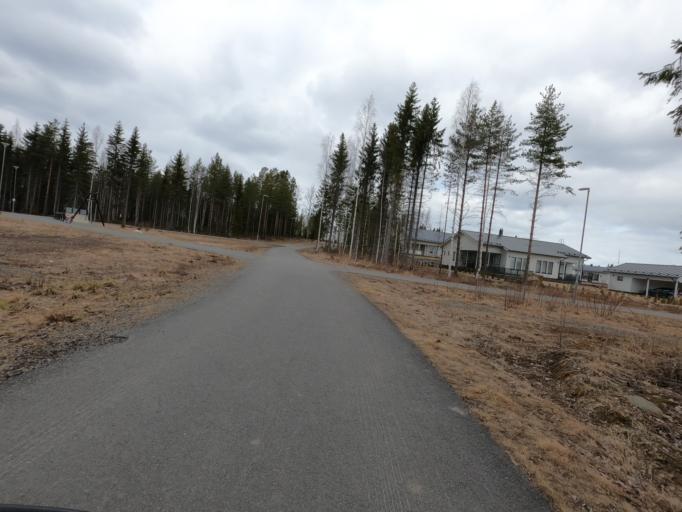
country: FI
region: North Karelia
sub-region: Joensuu
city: Joensuu
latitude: 62.5643
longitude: 29.8209
